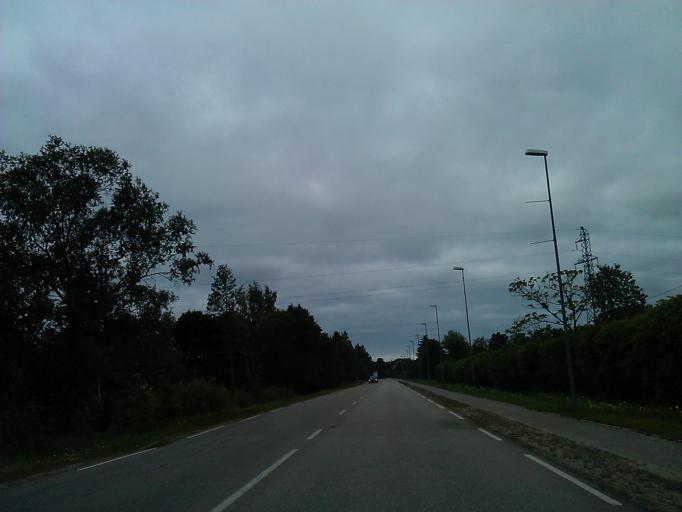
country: LV
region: Carnikava
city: Carnikava
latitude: 57.1270
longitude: 24.2922
